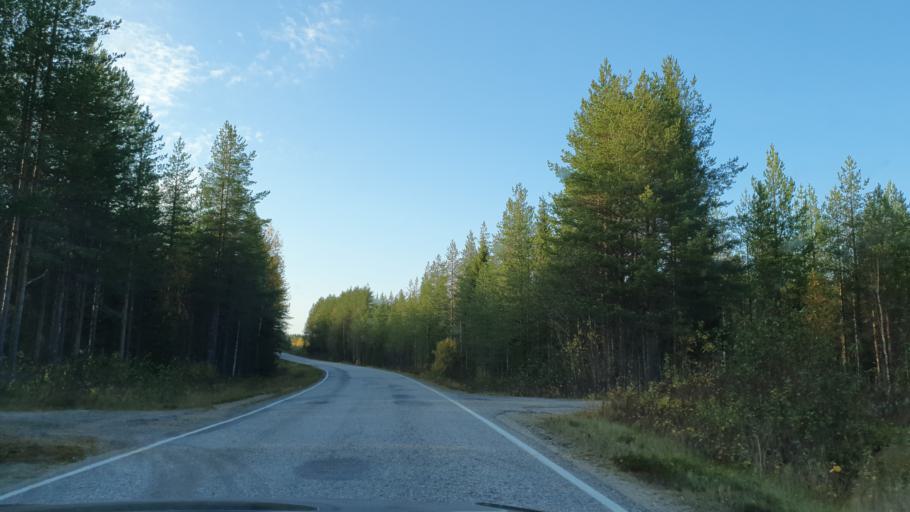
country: FI
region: Kainuu
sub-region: Kehys-Kainuu
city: Kuhmo
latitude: 64.2421
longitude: 29.4335
